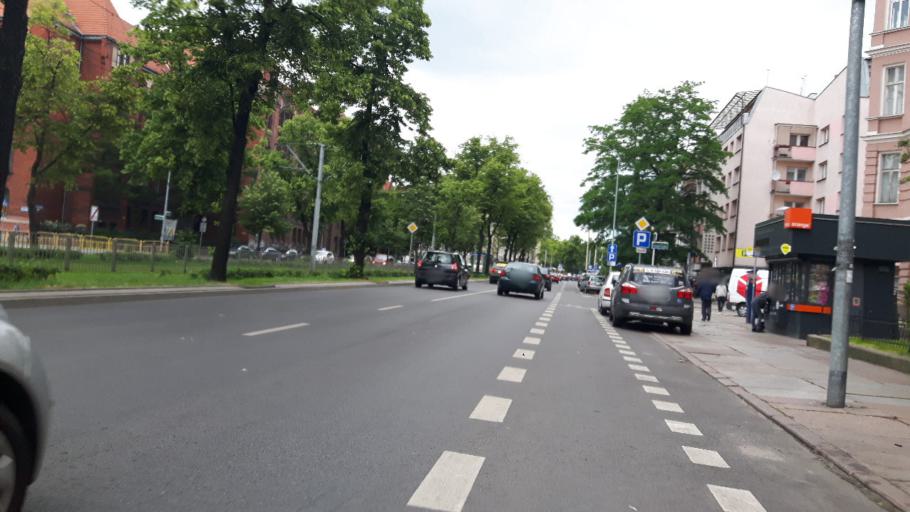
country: PL
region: West Pomeranian Voivodeship
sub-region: Szczecin
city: Szczecin
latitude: 53.4303
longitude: 14.5386
